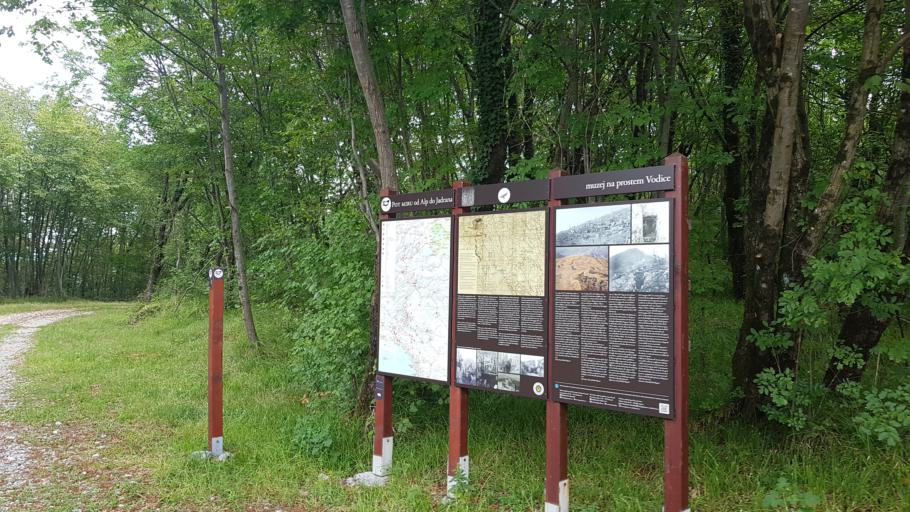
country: SI
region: Kanal
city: Deskle
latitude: 46.0153
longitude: 13.6346
